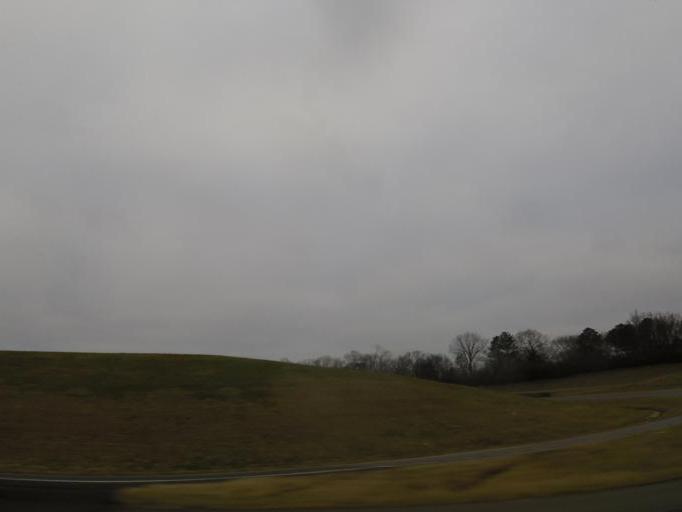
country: US
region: Alabama
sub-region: Jefferson County
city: Gardendale
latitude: 33.6731
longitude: -86.8300
